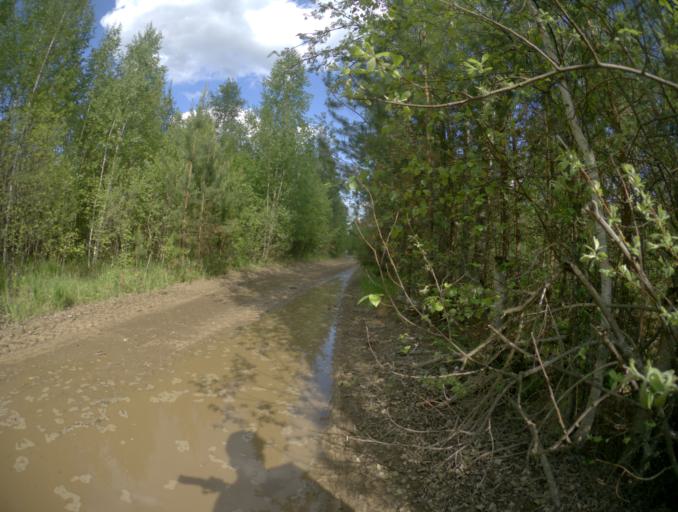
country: RU
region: Vladimir
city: Zolotkovo
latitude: 55.3298
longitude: 40.9600
